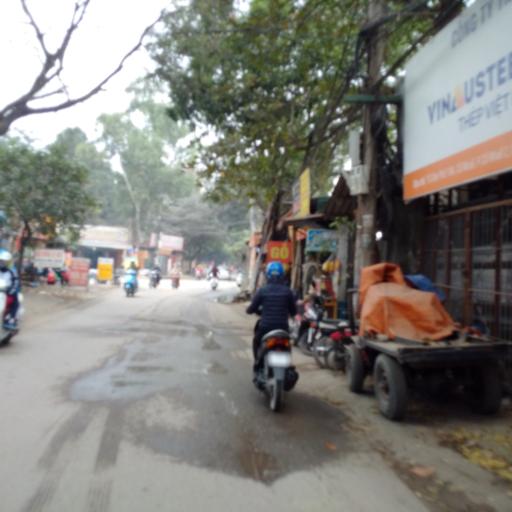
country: VN
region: Ha Noi
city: Cau Dien
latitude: 21.0708
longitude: 105.7772
